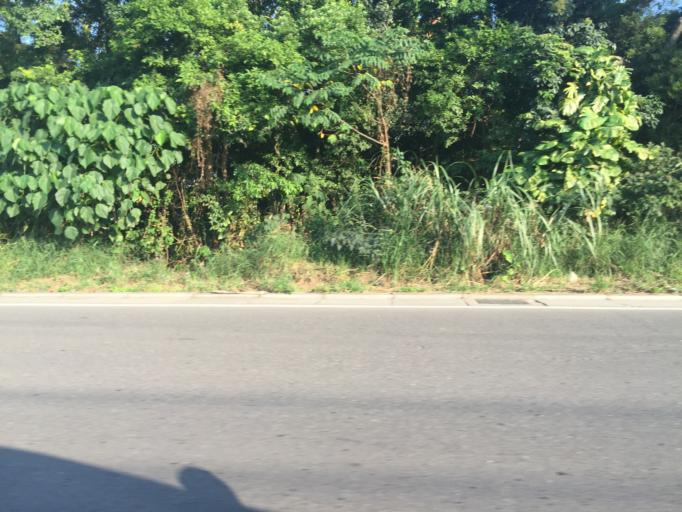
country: TW
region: Taiwan
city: Daxi
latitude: 24.9293
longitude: 121.2600
